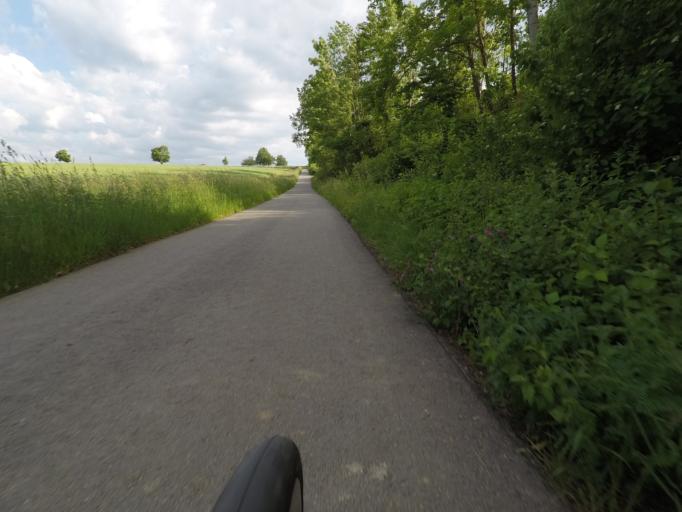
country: DE
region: Baden-Wuerttemberg
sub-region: Regierungsbezirk Stuttgart
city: Magstadt
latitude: 48.7012
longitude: 8.9512
